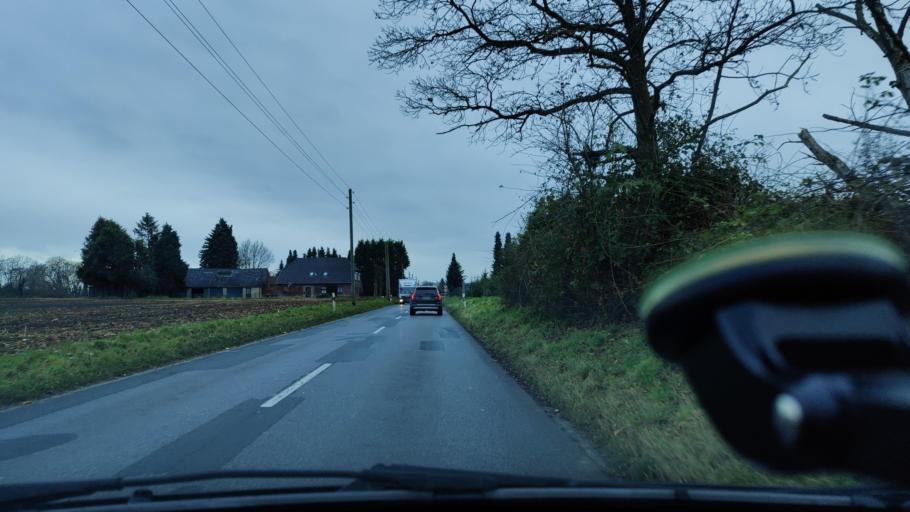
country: DE
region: North Rhine-Westphalia
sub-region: Regierungsbezirk Dusseldorf
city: Alpen
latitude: 51.5846
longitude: 6.4766
